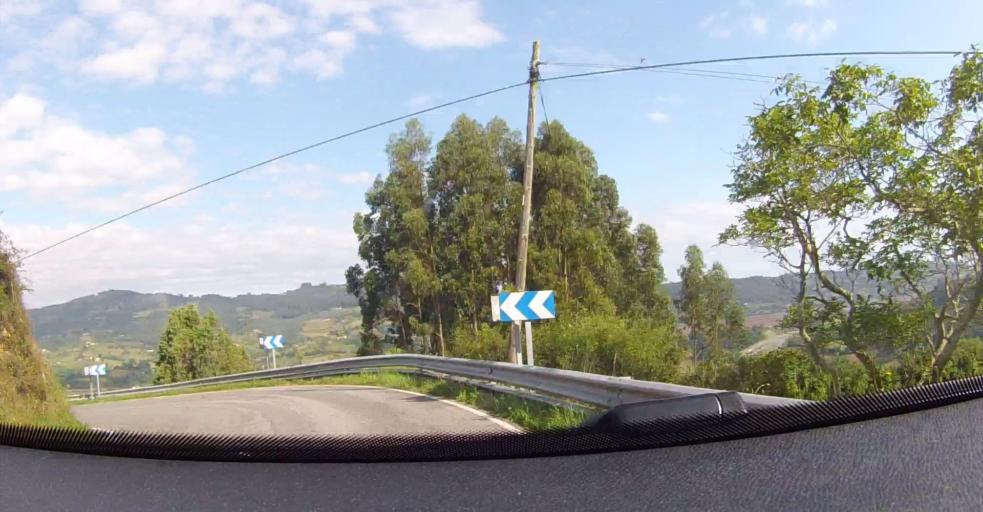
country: ES
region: Asturias
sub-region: Province of Asturias
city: Villaviciosa
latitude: 43.4864
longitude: -5.4145
